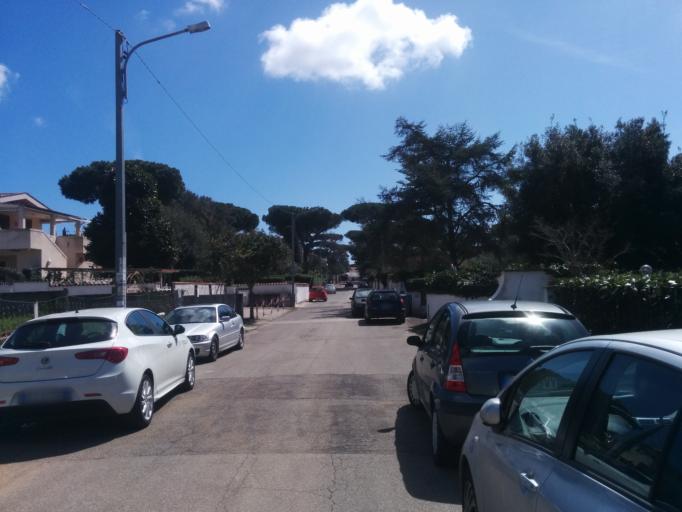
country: IT
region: Latium
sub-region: Citta metropolitana di Roma Capitale
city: Lavinio
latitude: 41.5016
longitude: 12.5949
